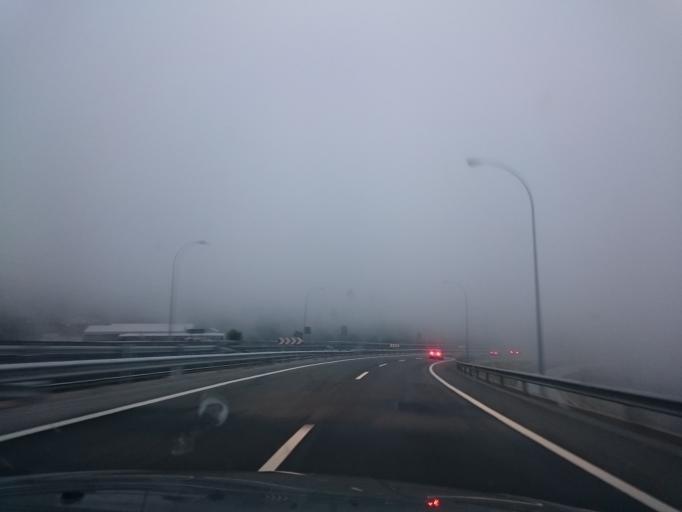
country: ES
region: Castille and Leon
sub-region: Provincia de Leon
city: Sena de Luna
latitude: 42.9805
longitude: -5.8311
